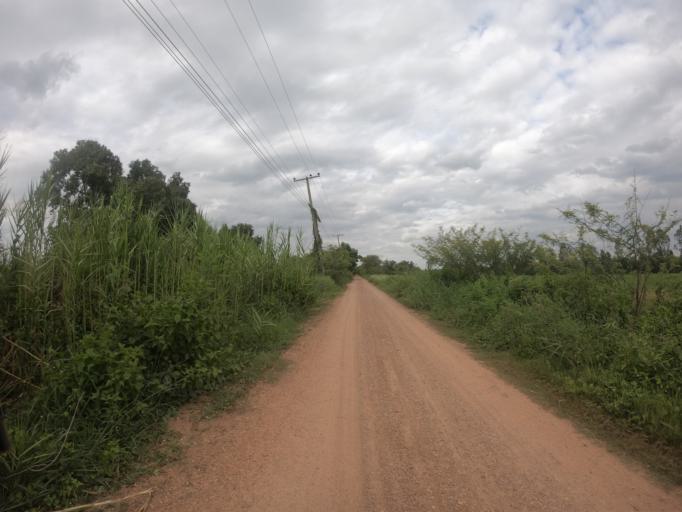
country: TH
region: Pathum Thani
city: Nong Suea
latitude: 14.0762
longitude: 100.8402
